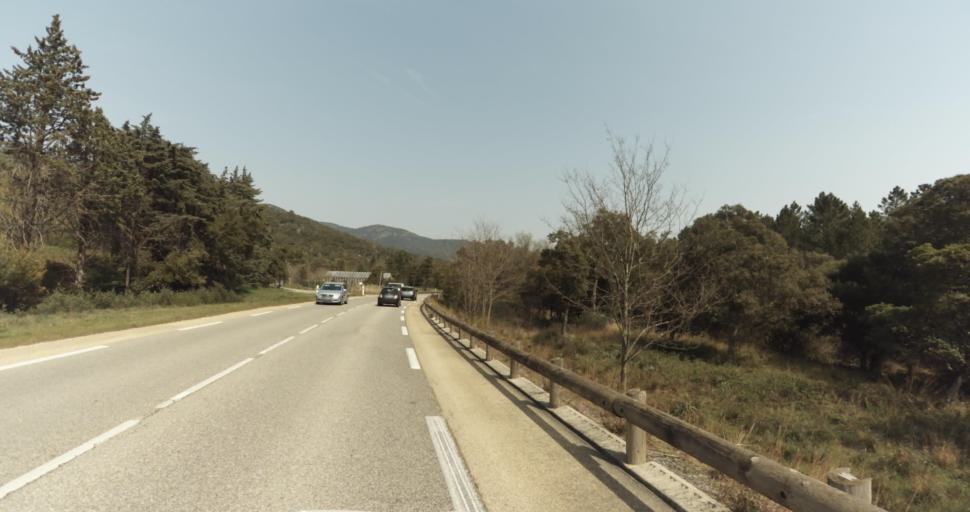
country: FR
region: Provence-Alpes-Cote d'Azur
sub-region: Departement du Var
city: Le Lavandou
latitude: 43.1937
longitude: 6.3785
